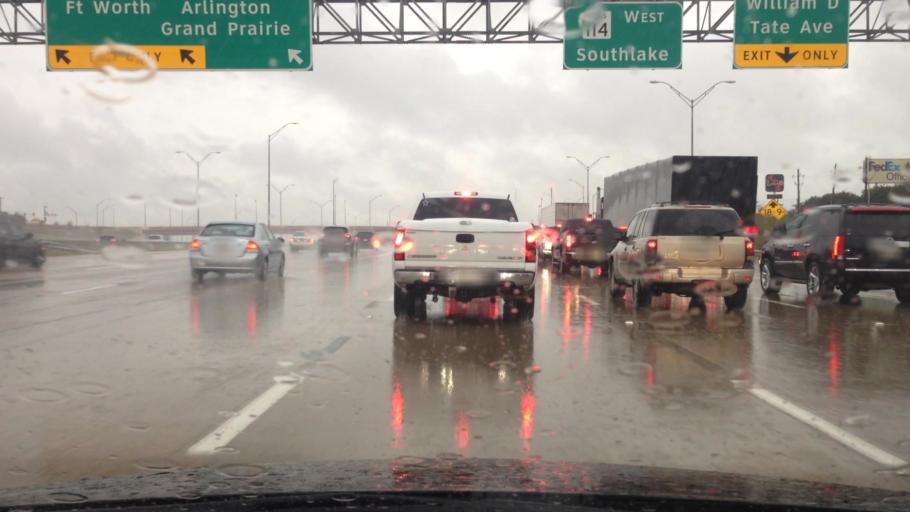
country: US
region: Texas
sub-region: Tarrant County
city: Grapevine
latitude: 32.9233
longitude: -97.0741
